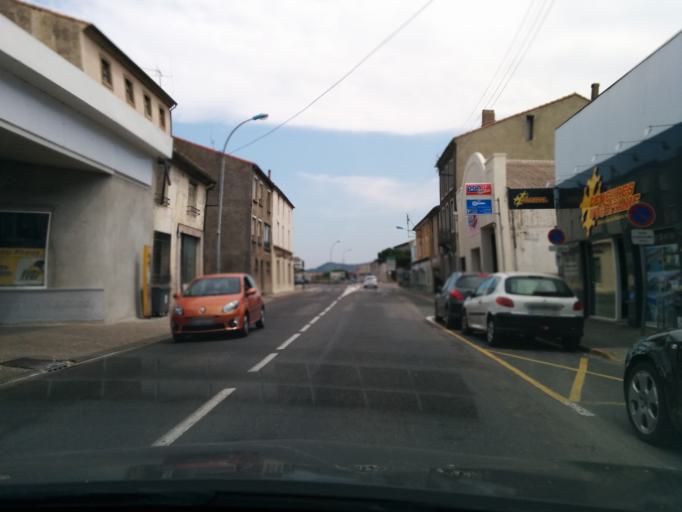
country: FR
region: Languedoc-Roussillon
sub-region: Departement de l'Aude
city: Carcassonne
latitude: 43.2184
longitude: 2.3439
